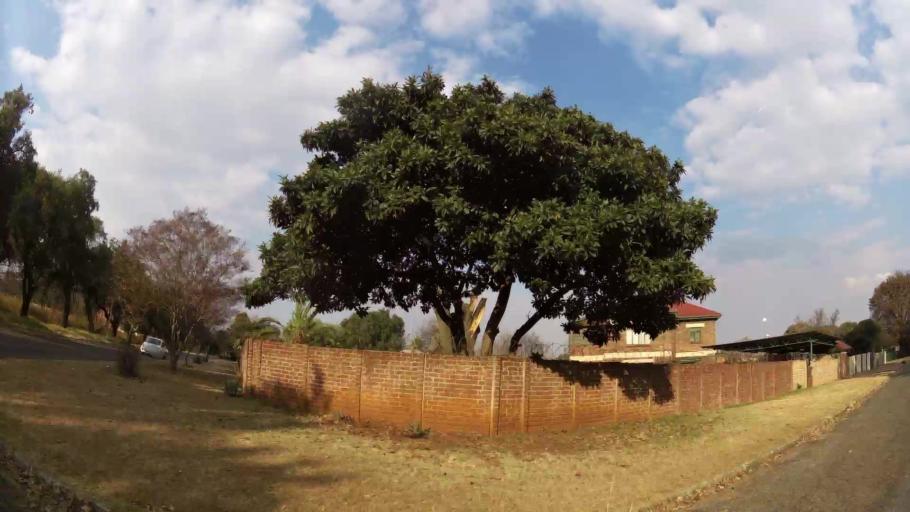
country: ZA
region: Gauteng
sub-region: Ekurhuleni Metropolitan Municipality
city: Springs
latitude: -26.2743
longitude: 28.4459
